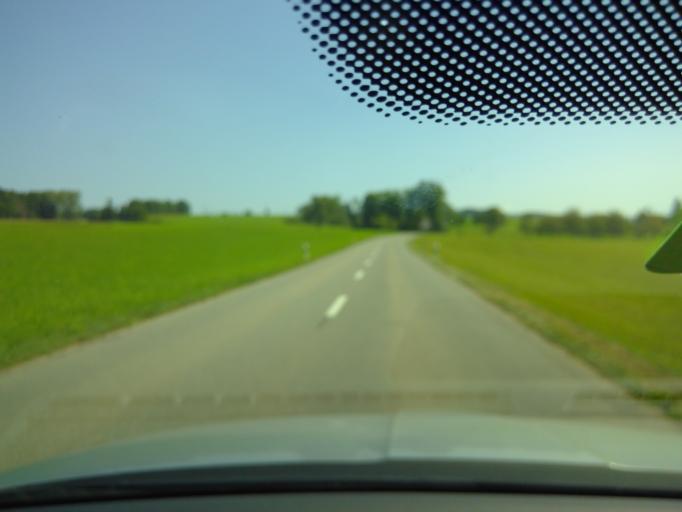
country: CH
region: Aargau
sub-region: Bezirk Kulm
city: Menziken
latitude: 47.2301
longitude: 8.1959
